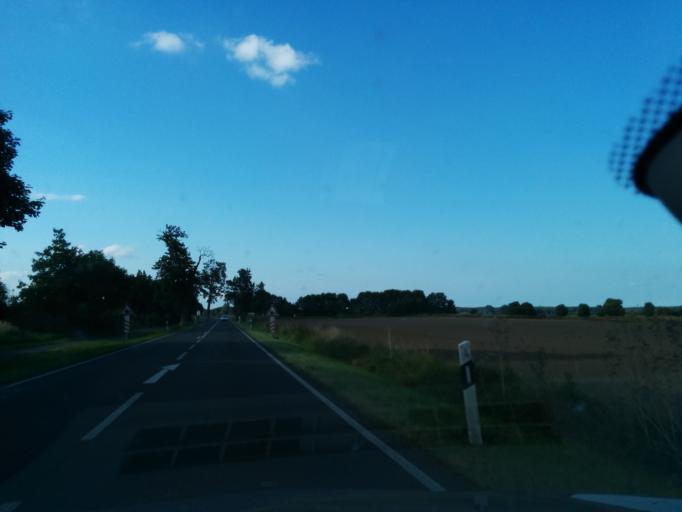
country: DE
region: Mecklenburg-Vorpommern
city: Pasewalk
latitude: 53.5316
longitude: 13.9744
